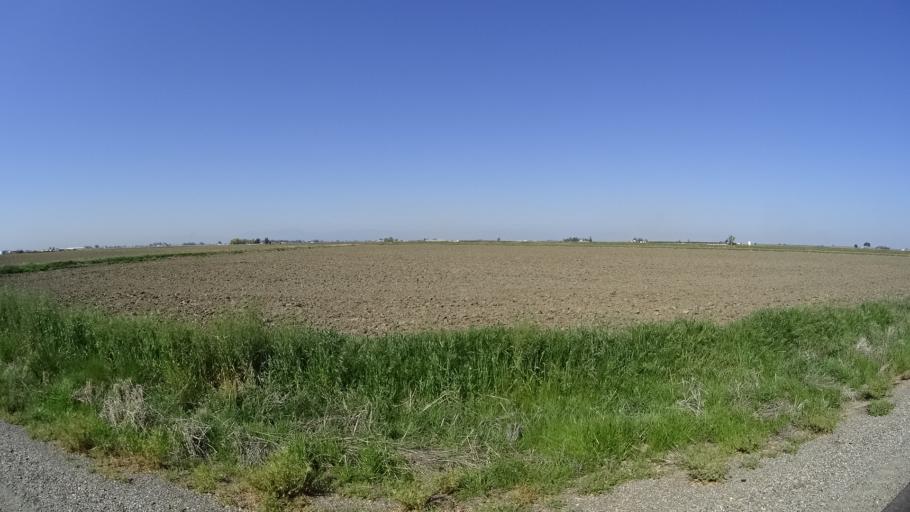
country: US
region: California
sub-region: Glenn County
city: Willows
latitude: 39.5912
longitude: -122.0651
